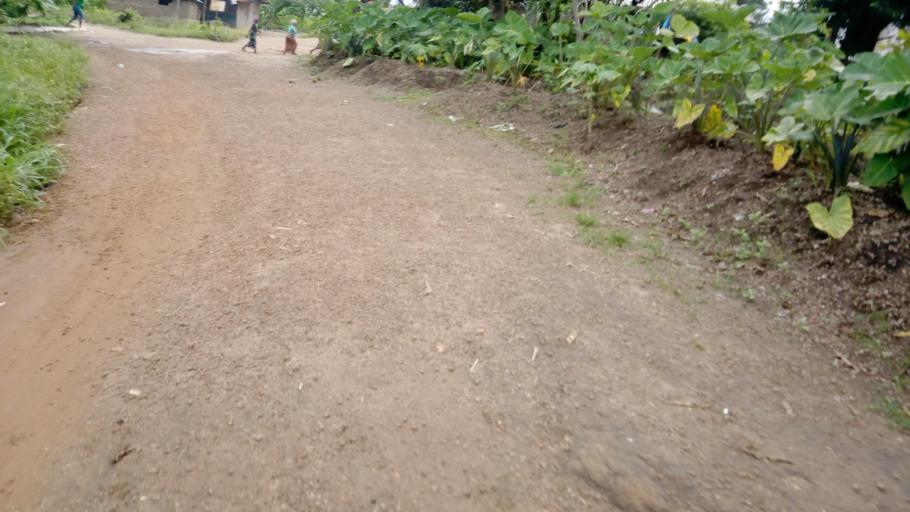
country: SL
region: Northern Province
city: Makeni
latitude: 8.8983
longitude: -12.0279
